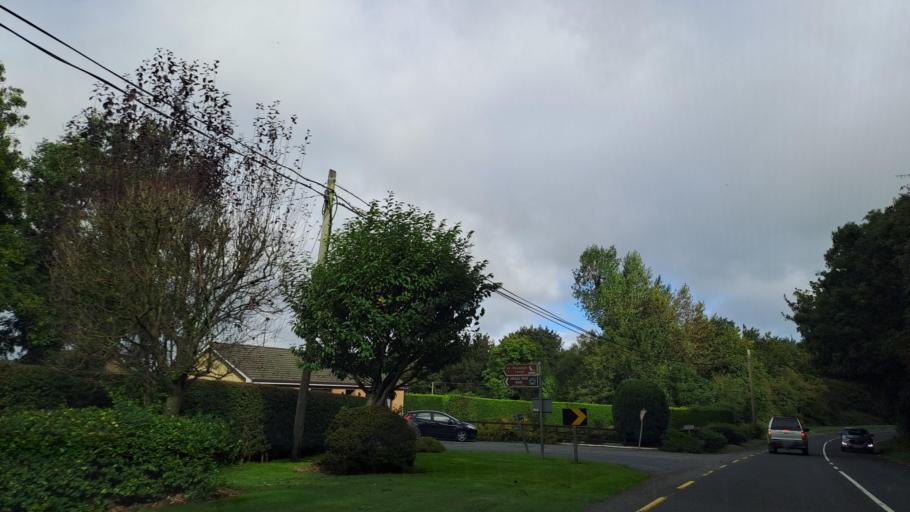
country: IE
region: Ulster
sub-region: County Monaghan
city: Carrickmacross
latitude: 53.9597
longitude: -6.7519
